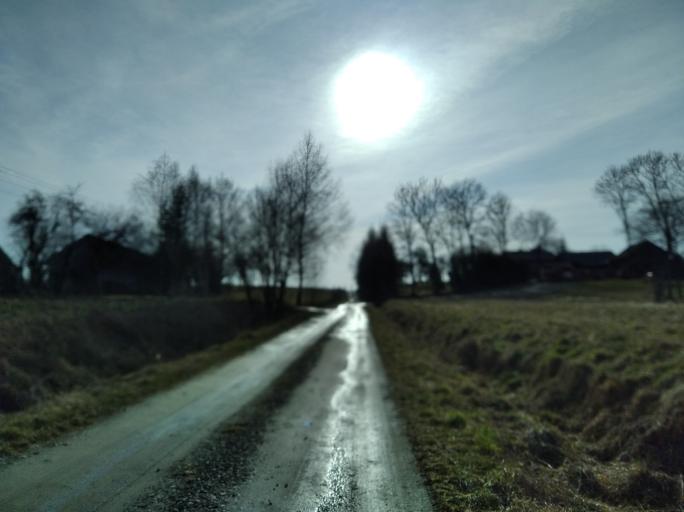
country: PL
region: Subcarpathian Voivodeship
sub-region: Powiat brzozowski
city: Gorki
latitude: 49.6533
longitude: 22.0470
